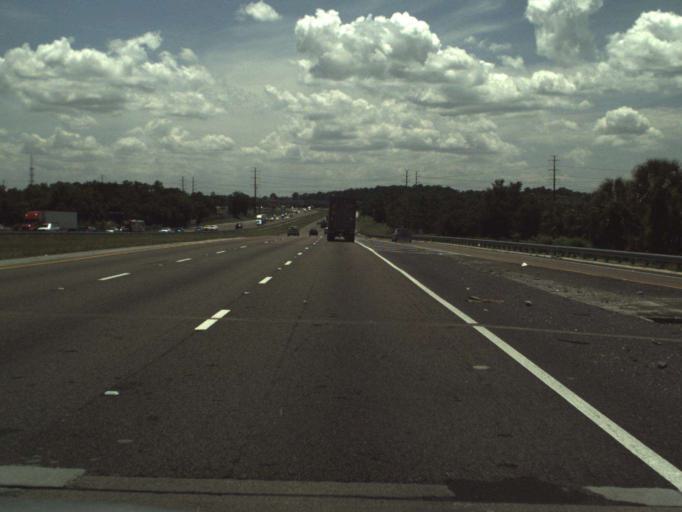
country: US
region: Florida
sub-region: Volusia County
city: DeBary
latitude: 28.8297
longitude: -81.3255
